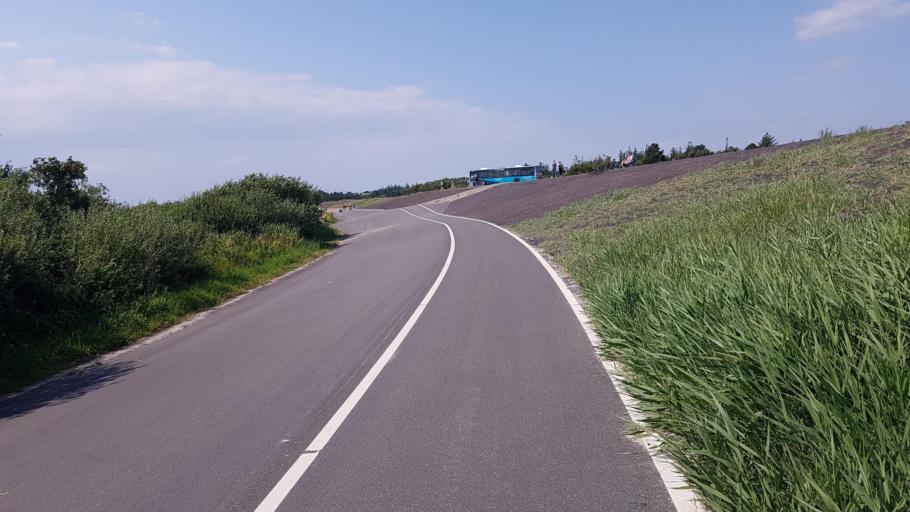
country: DE
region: Schleswig-Holstein
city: Sankt Peter-Ording
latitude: 54.3016
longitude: 8.6317
